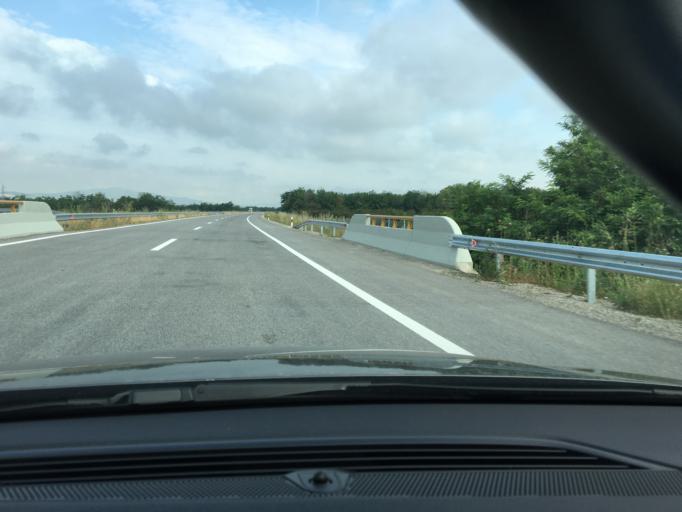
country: MK
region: Sveti Nikole
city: Sveti Nikole
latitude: 41.8332
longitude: 21.9910
